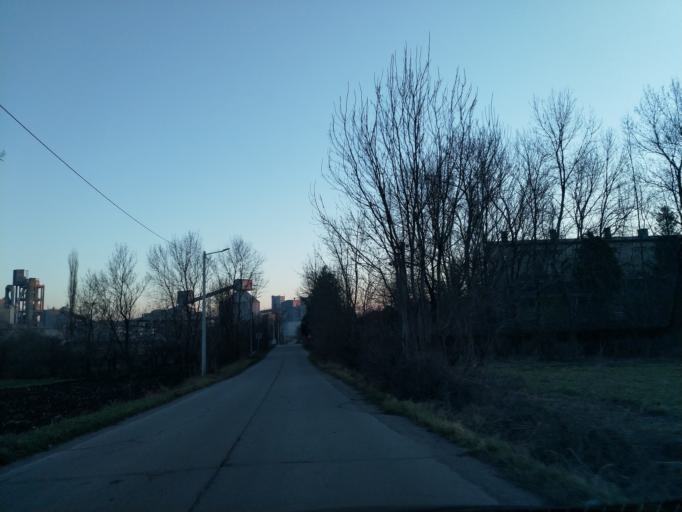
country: RS
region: Central Serbia
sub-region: Pomoravski Okrug
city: Paracin
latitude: 43.9147
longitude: 21.5107
